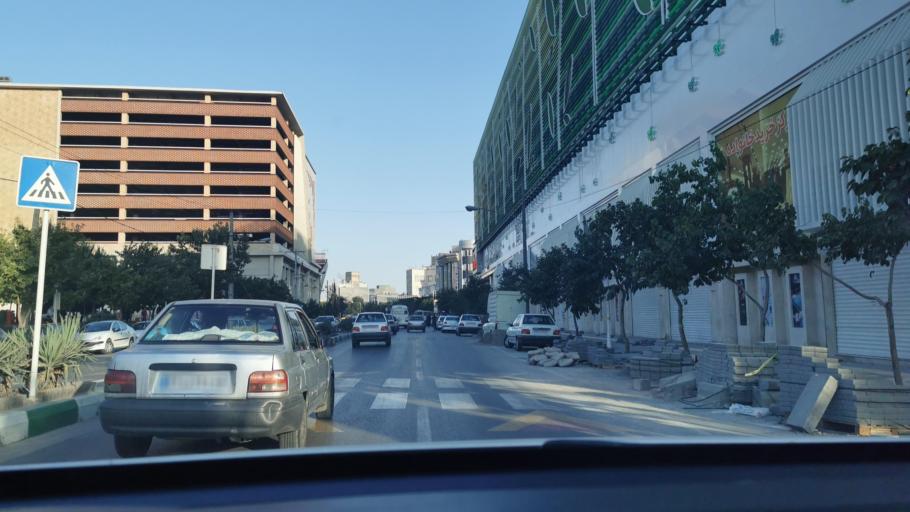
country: IR
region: Razavi Khorasan
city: Mashhad
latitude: 36.2926
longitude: 59.6467
